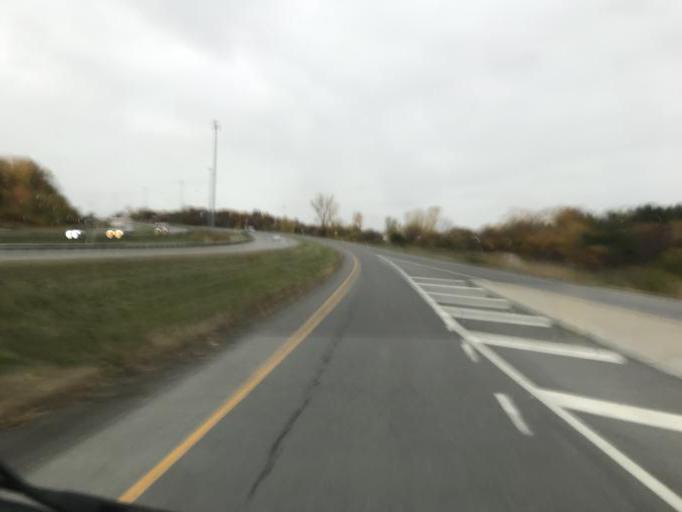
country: CA
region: Quebec
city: Bois-des-Filion
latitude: 45.6731
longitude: -73.7635
